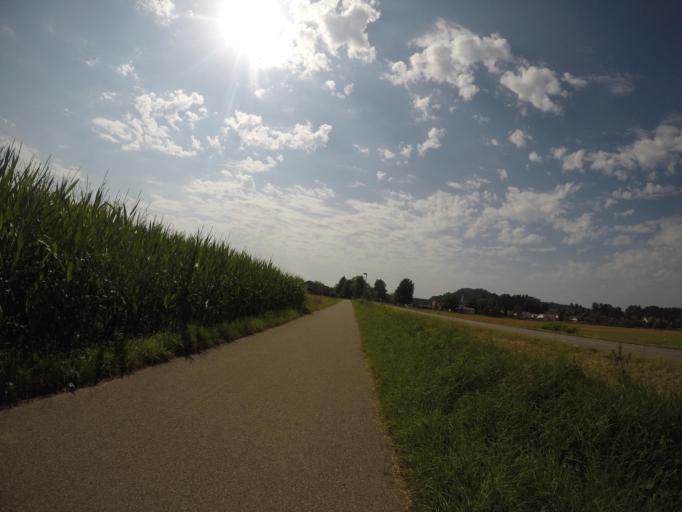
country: DE
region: Baden-Wuerttemberg
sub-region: Tuebingen Region
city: Kirchberg an der Iller
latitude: 48.1687
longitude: 10.0787
